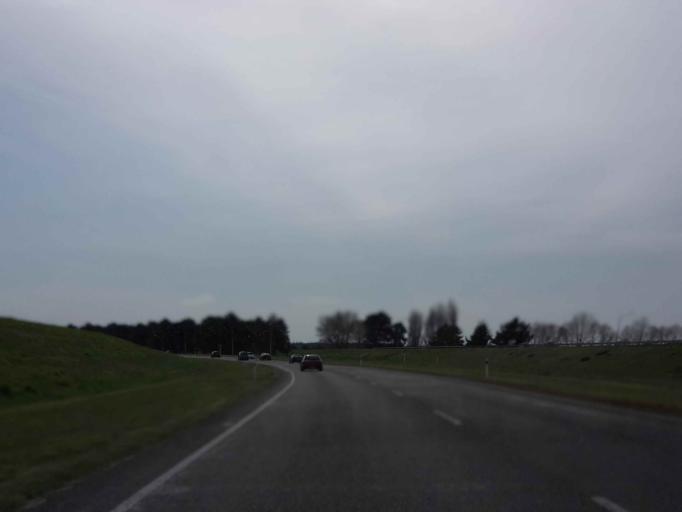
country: NZ
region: Canterbury
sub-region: Waimakariri District
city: Kaiapoi
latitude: -43.4300
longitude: 172.6444
